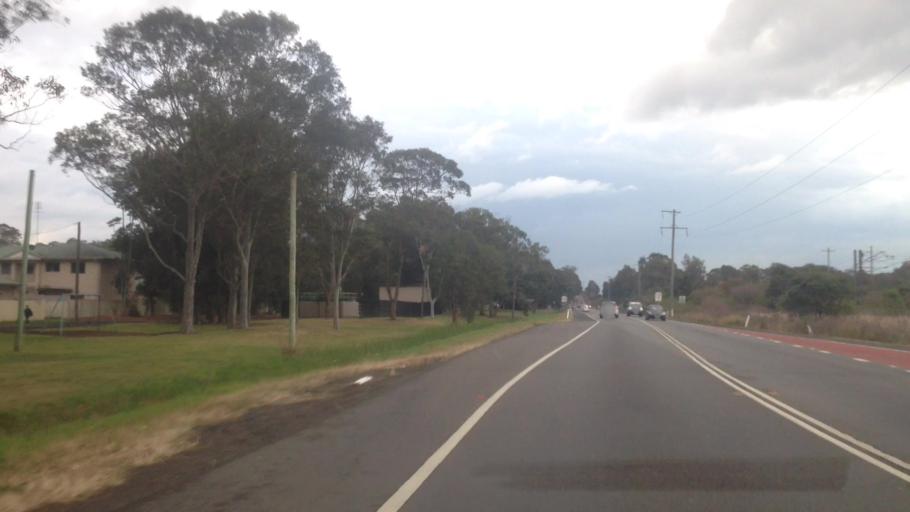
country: AU
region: New South Wales
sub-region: Wyong Shire
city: Chittaway Bay
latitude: -33.2794
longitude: 151.4272
